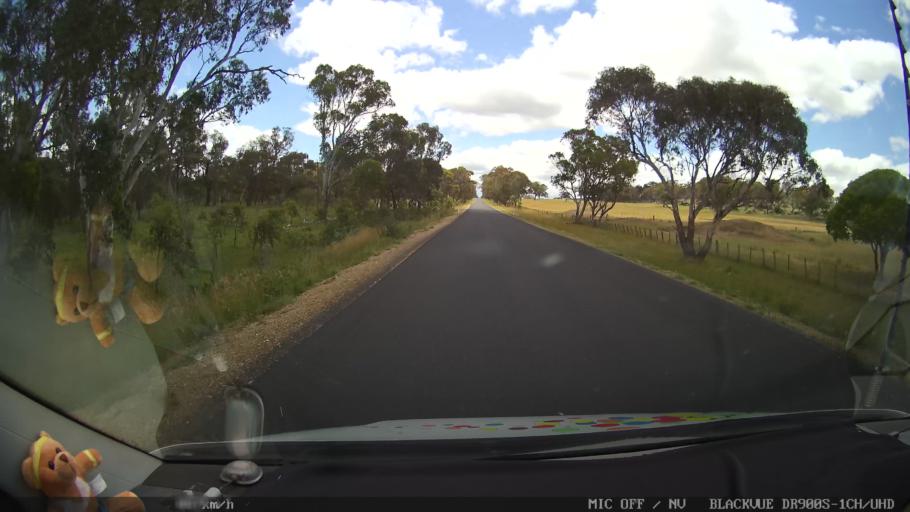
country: AU
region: New South Wales
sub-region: Glen Innes Severn
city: Glen Innes
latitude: -29.4237
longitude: 151.7069
